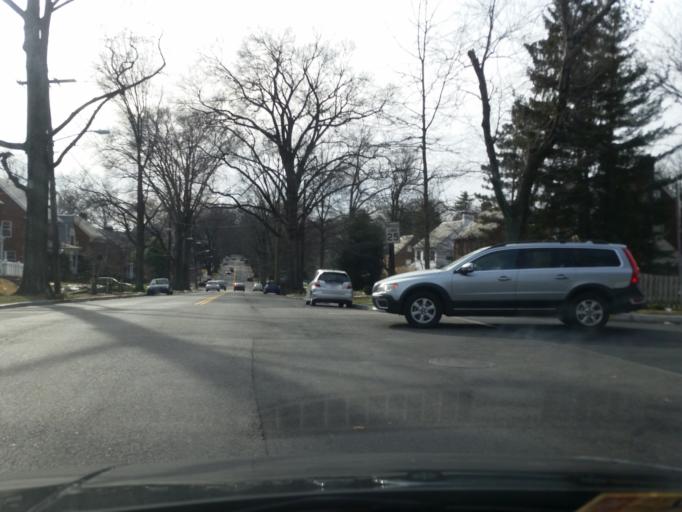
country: US
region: Maryland
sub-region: Montgomery County
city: Chevy Chase
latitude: 38.9719
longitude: -77.0715
